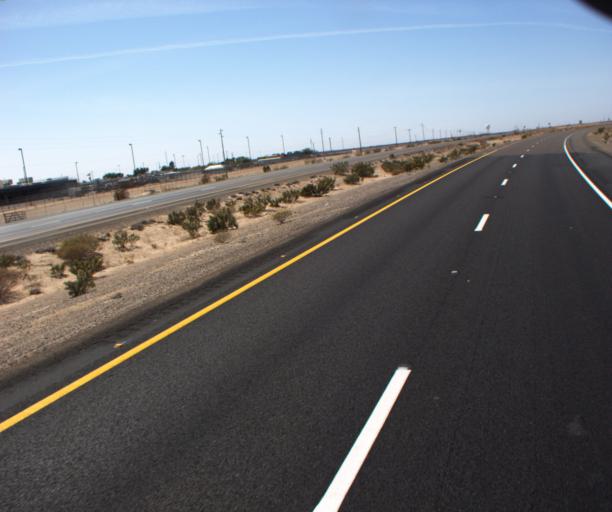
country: US
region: Arizona
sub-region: Yuma County
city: Somerton
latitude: 32.4954
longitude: -114.6388
